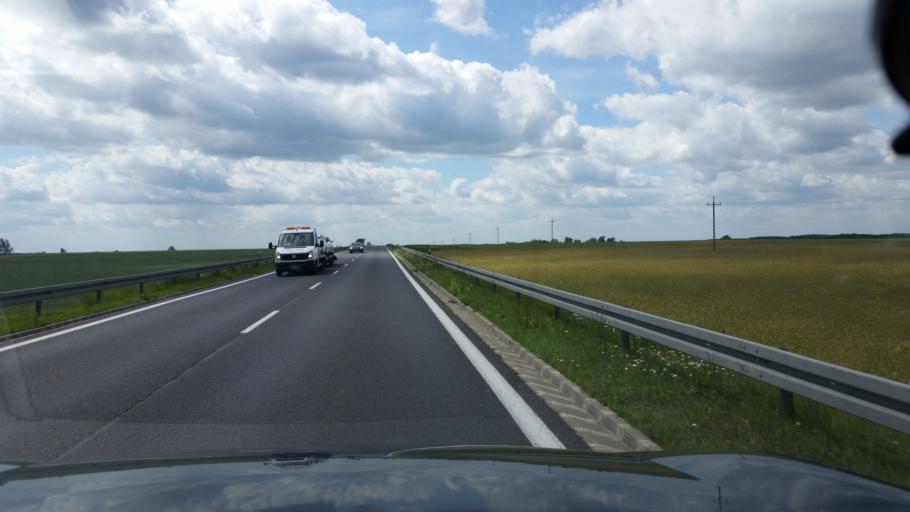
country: PL
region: Podlasie
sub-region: Powiat kolnenski
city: Stawiski
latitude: 53.4132
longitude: 22.1628
